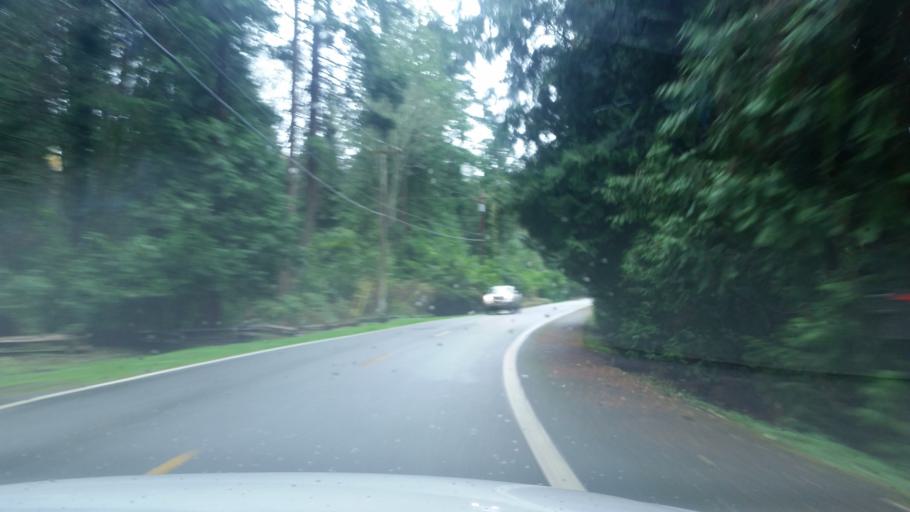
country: US
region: Washington
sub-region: Snohomish County
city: Woodway
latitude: 47.7987
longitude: -122.3803
